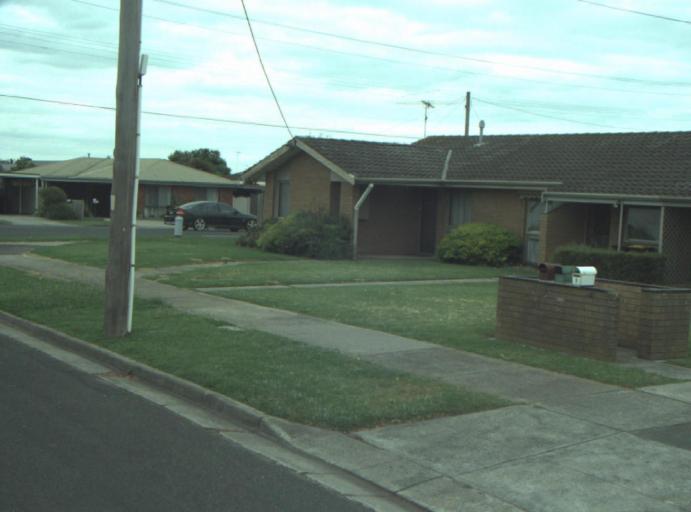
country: AU
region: Victoria
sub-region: Greater Geelong
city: Breakwater
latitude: -38.1970
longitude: 144.3388
